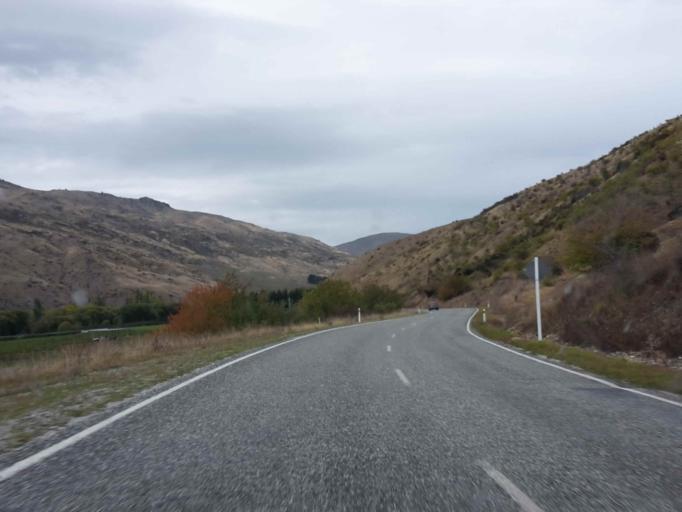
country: NZ
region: Otago
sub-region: Queenstown-Lakes District
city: Wanaka
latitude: -44.8226
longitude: 169.0620
